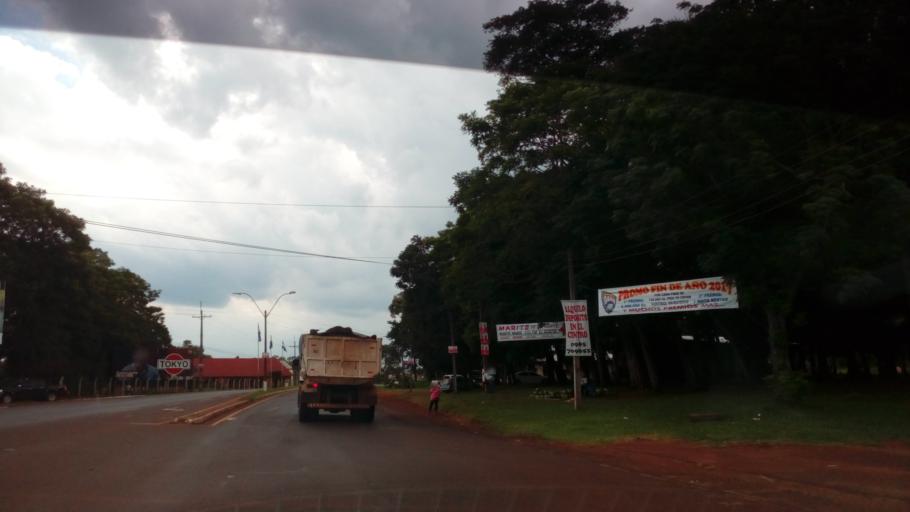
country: PY
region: Itapua
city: Obligado
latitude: -27.0727
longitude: -55.6391
